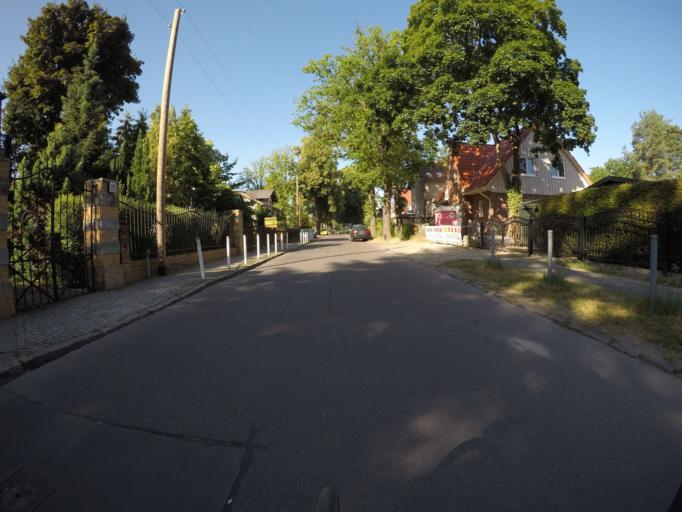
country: DE
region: Berlin
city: Schmockwitz
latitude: 52.3474
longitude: 13.6427
